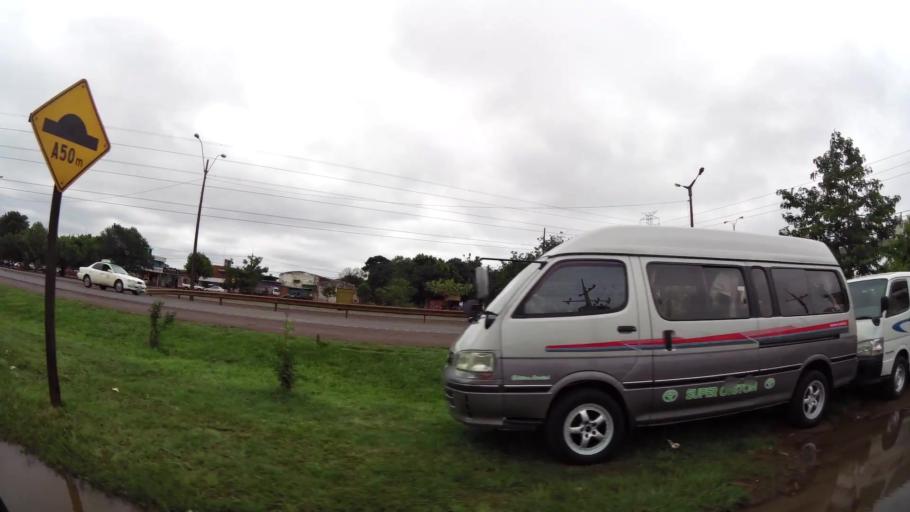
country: PY
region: Alto Parana
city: Ciudad del Este
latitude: -25.4961
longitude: -54.6860
